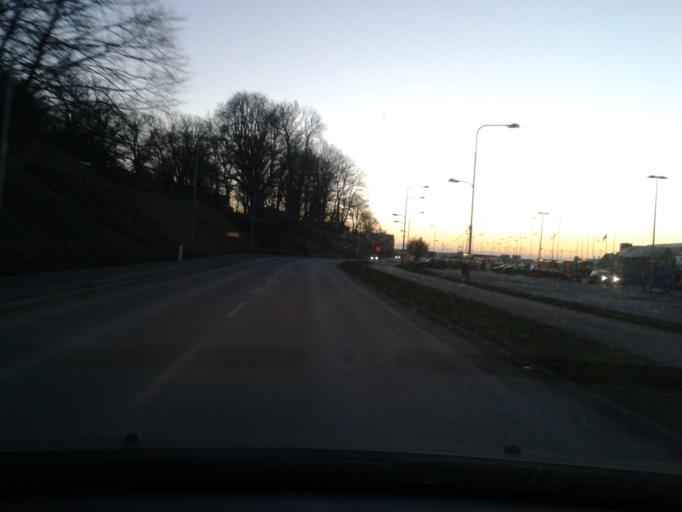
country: SE
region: Gotland
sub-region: Gotland
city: Visby
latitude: 57.6354
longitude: 18.2842
